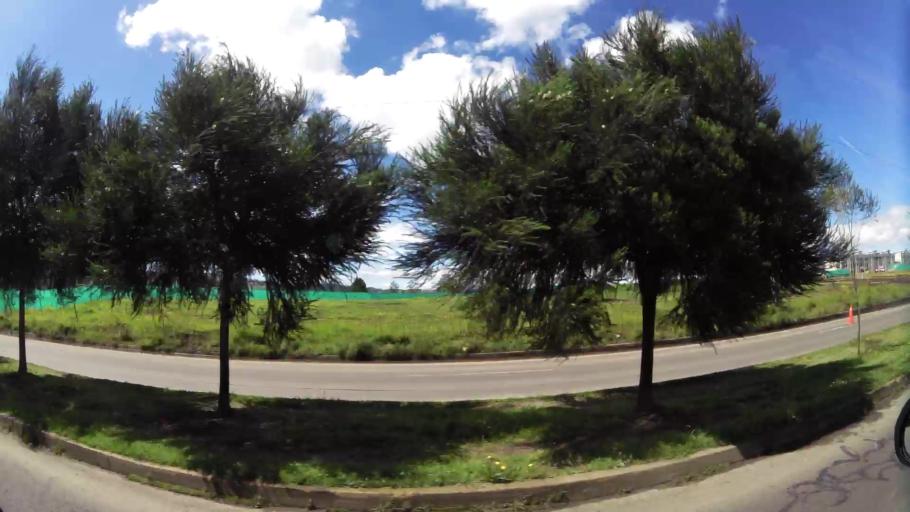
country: EC
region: Pichincha
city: Quito
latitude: -0.2979
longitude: -78.5538
